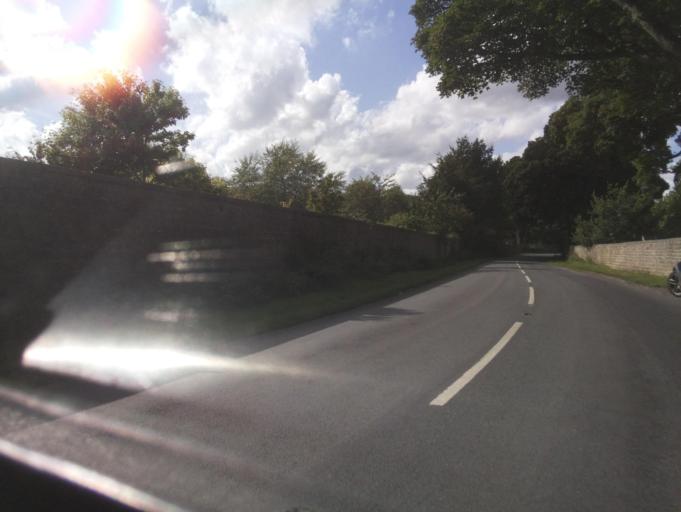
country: GB
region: England
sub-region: North Yorkshire
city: Leyburn
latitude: 54.2674
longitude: -1.7423
